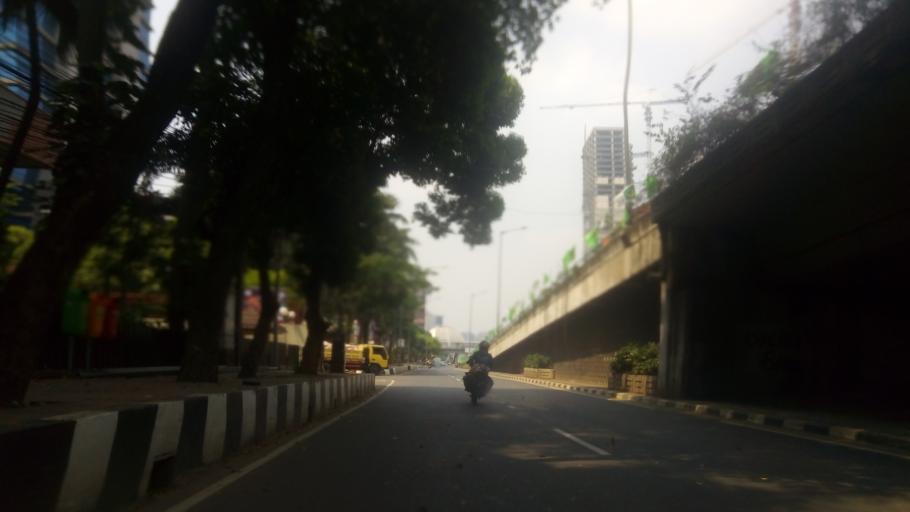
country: ID
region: Jakarta Raya
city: Jakarta
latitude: -6.2370
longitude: 106.8285
